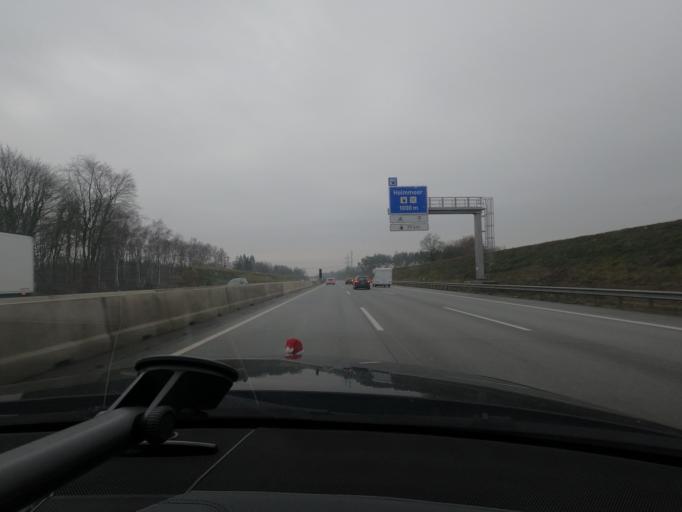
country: DE
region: Schleswig-Holstein
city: Ellerau
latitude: 53.7301
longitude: 9.9414
